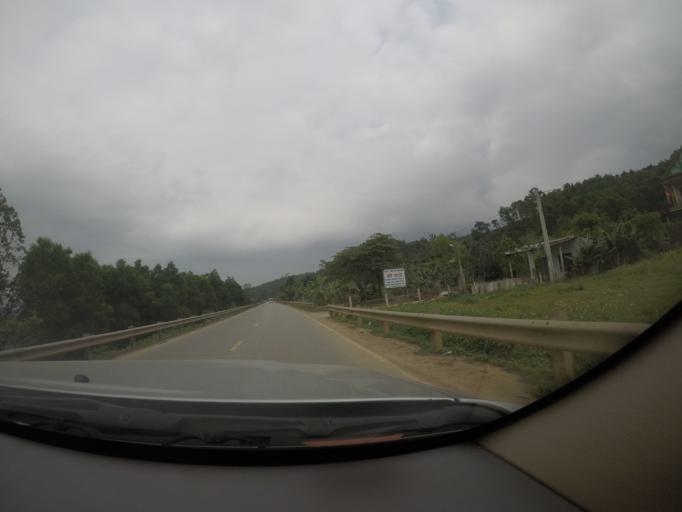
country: VN
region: Quang Binh
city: Ba Don
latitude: 17.6076
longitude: 106.3420
